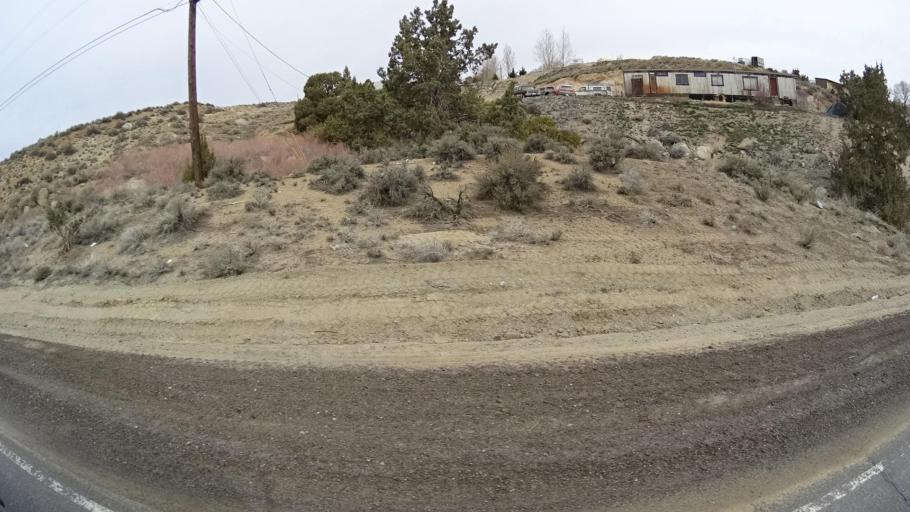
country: US
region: Nevada
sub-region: Washoe County
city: Sun Valley
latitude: 39.6012
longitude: -119.7979
